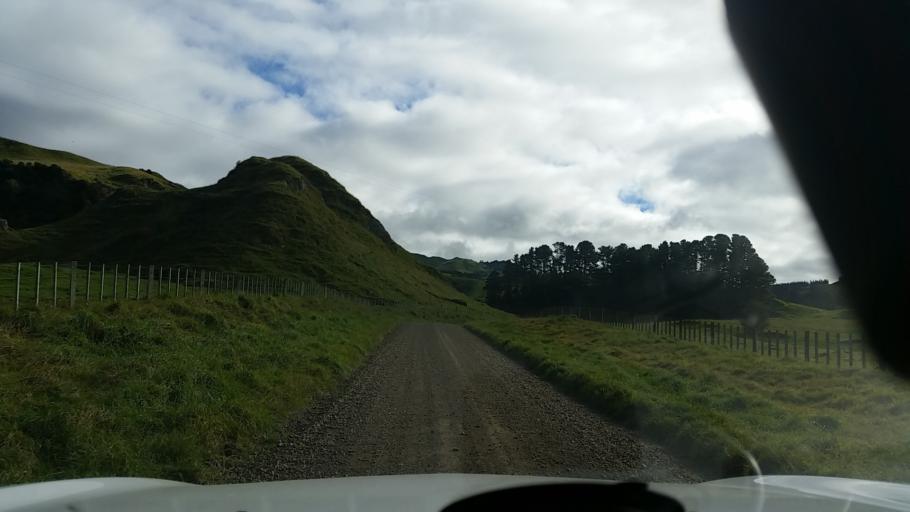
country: NZ
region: Hawke's Bay
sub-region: Napier City
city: Napier
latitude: -39.0989
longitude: 176.8733
